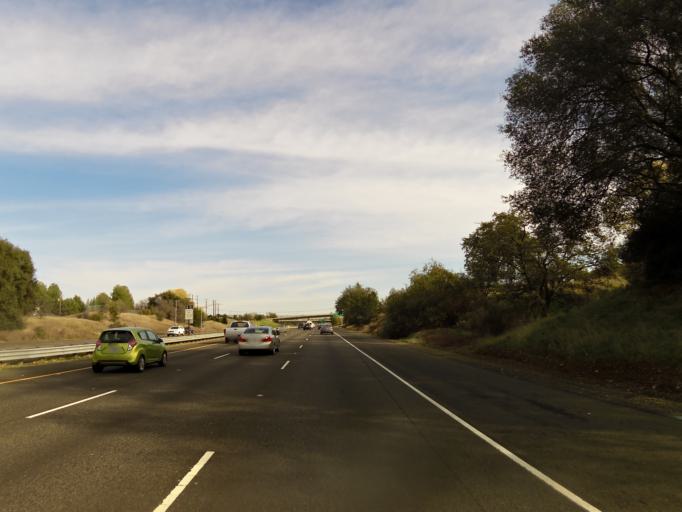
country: US
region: California
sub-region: Sacramento County
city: Folsom
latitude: 38.6423
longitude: -121.1643
